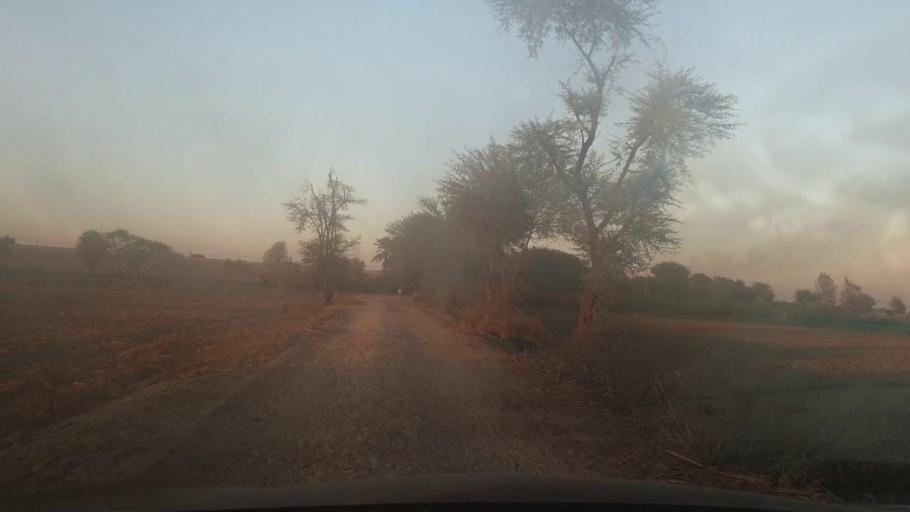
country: PK
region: Sindh
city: Ghotki
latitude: 28.0580
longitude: 69.3676
